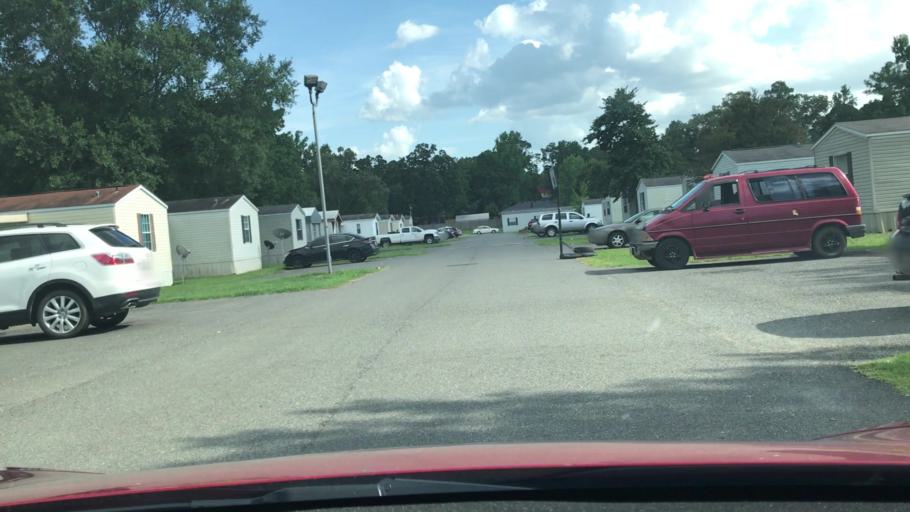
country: US
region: Louisiana
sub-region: De Soto Parish
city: Stonewall
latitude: 32.3894
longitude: -93.7660
